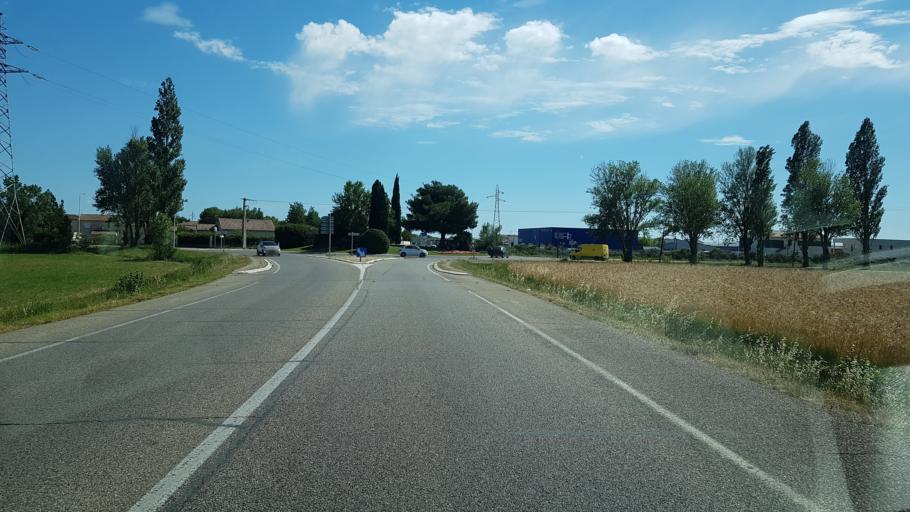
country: FR
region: Provence-Alpes-Cote d'Azur
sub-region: Departement des Bouches-du-Rhone
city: Saint-Martin-de-Crau
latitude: 43.6439
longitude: 4.8002
